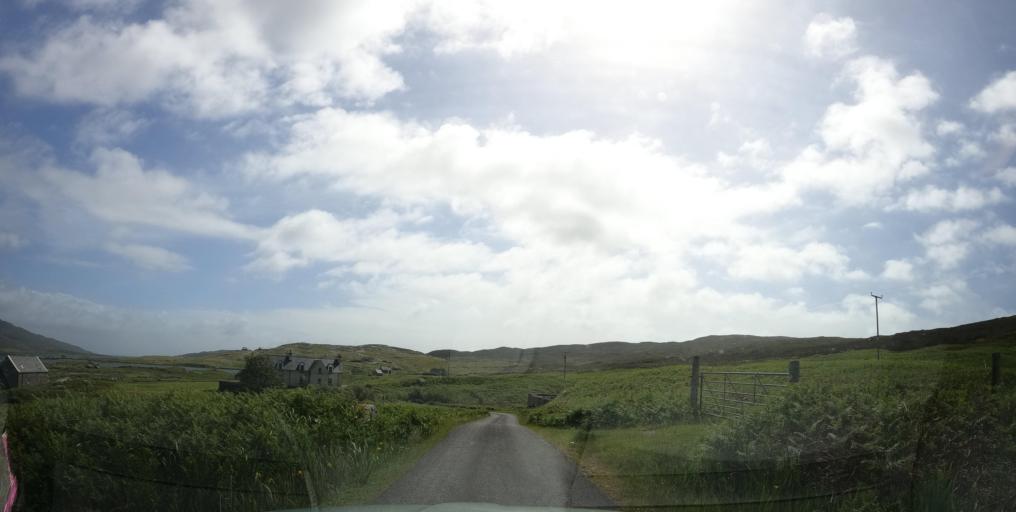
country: GB
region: Scotland
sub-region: Eilean Siar
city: Isle of South Uist
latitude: 57.1369
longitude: -7.3398
